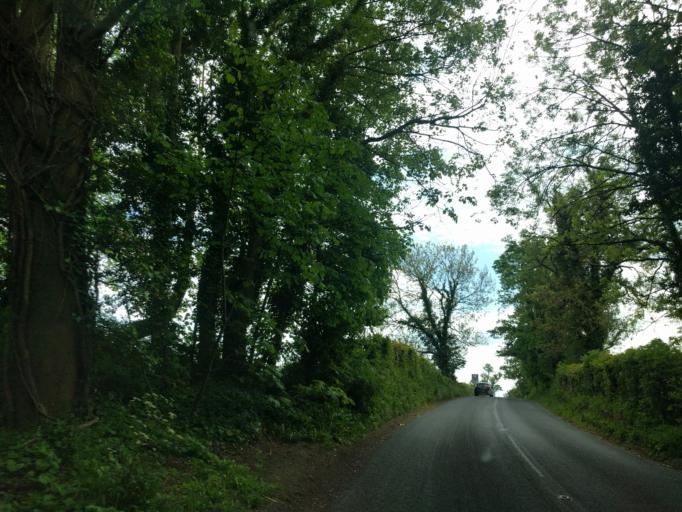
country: GB
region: England
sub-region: Wiltshire
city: Chippenham
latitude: 51.5049
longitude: -2.0983
